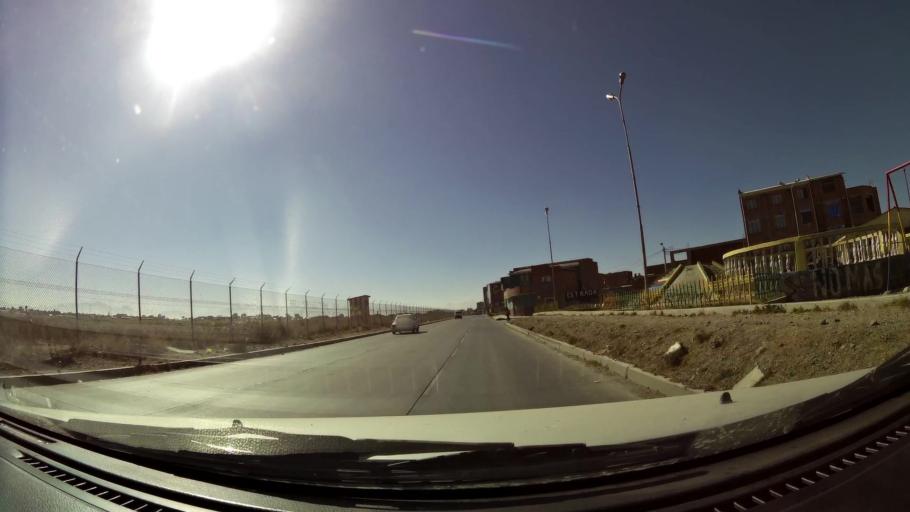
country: BO
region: La Paz
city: La Paz
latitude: -16.5161
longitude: -68.1791
